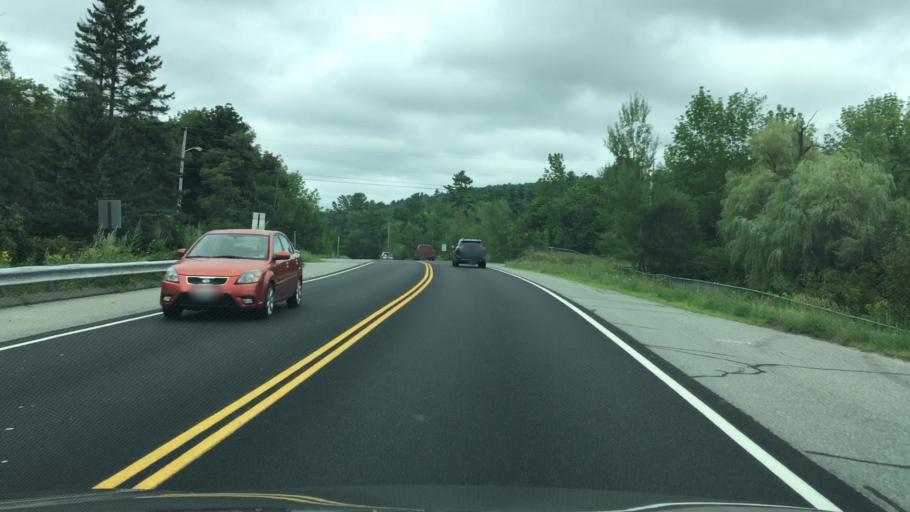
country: US
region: Maine
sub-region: Penobscot County
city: Orrington
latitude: 44.6893
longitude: -68.8107
